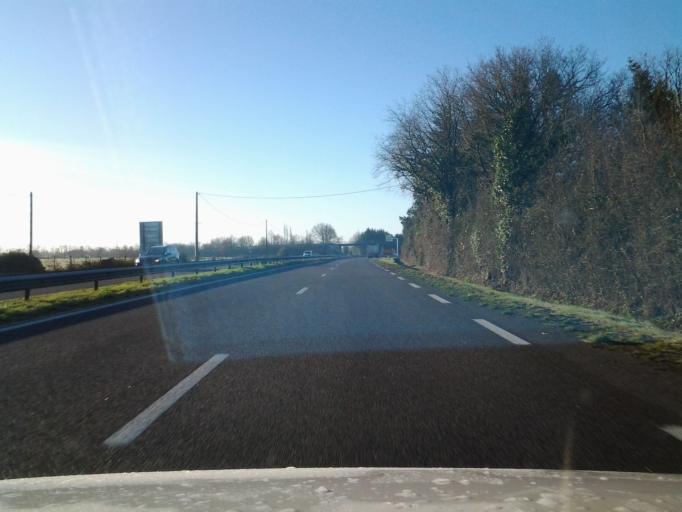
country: FR
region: Pays de la Loire
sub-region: Departement de la Vendee
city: Saligny
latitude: 46.8152
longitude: -1.4307
